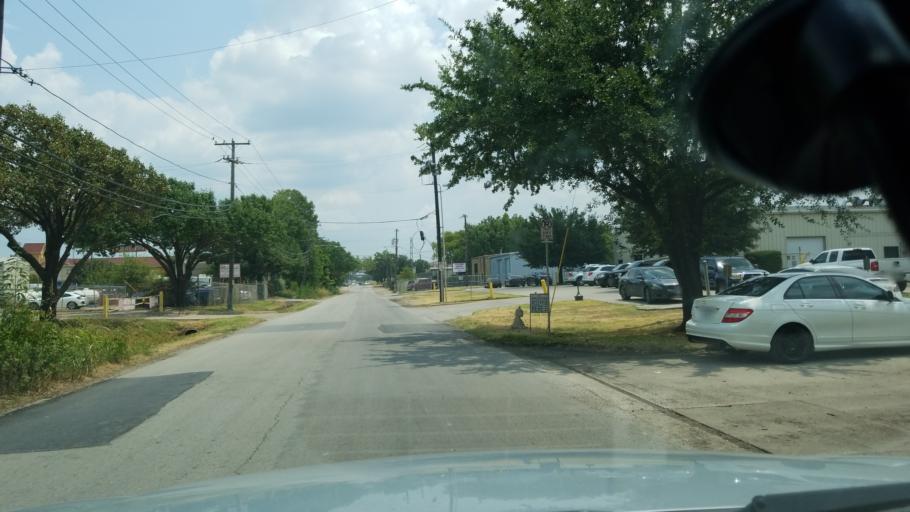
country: US
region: Texas
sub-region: Dallas County
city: Farmers Branch
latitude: 32.8666
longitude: -96.9110
